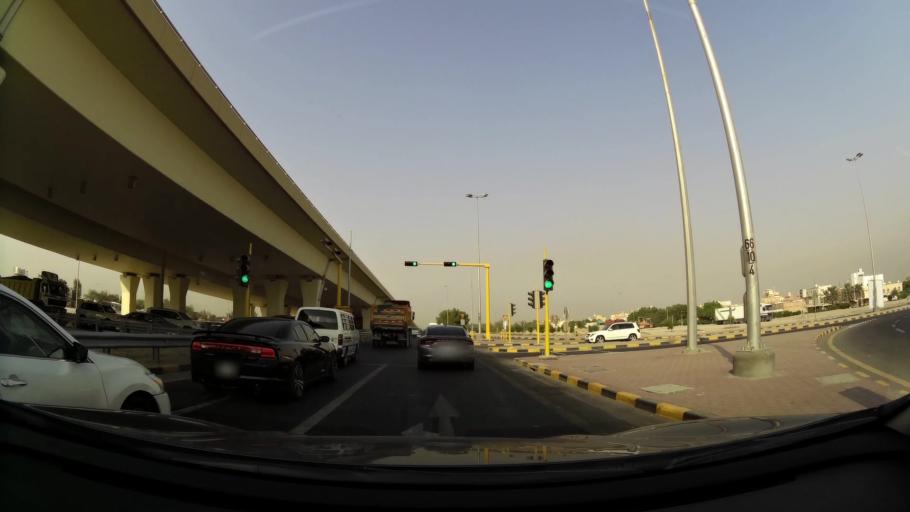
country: KW
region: Al Asimah
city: Ar Rabiyah
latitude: 29.3115
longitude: 47.8293
